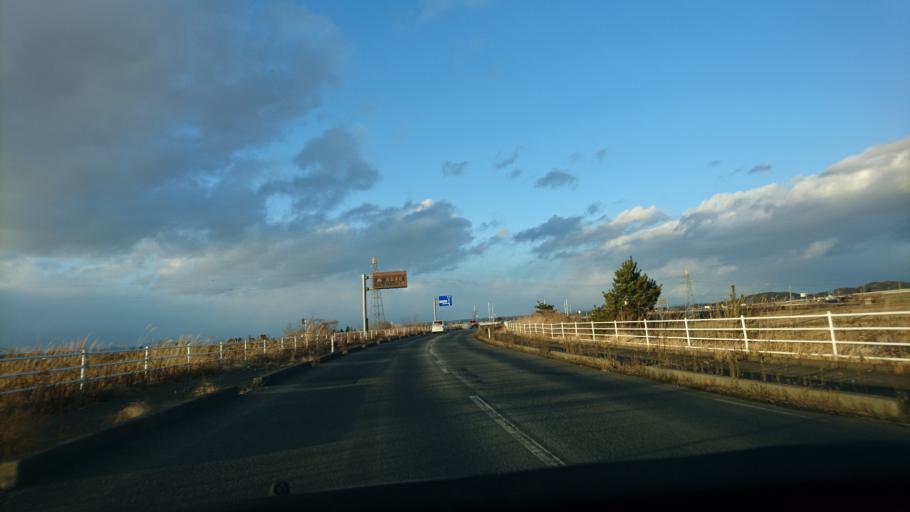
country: JP
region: Miyagi
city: Wakuya
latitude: 38.7254
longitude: 141.1485
